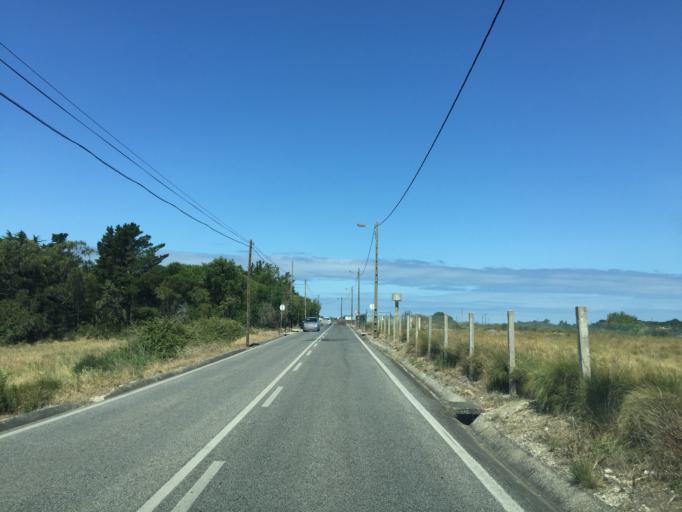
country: PT
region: Lisbon
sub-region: Sintra
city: Colares
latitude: 38.8253
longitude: -9.4285
